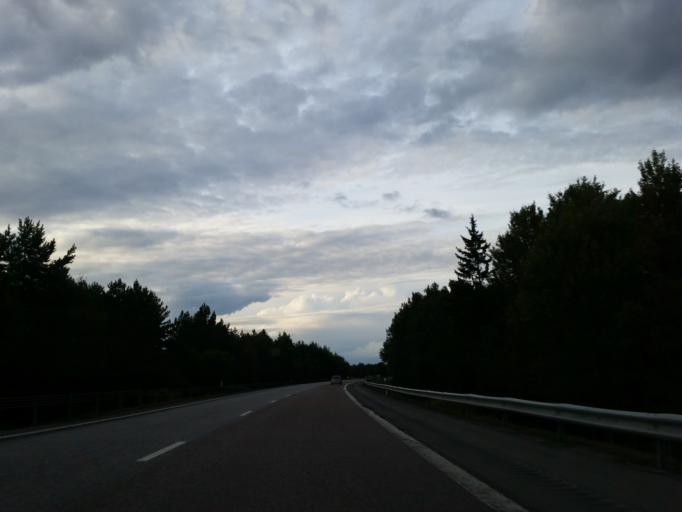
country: SE
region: Uppsala
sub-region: Knivsta Kommun
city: Knivsta
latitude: 59.7656
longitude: 17.7916
